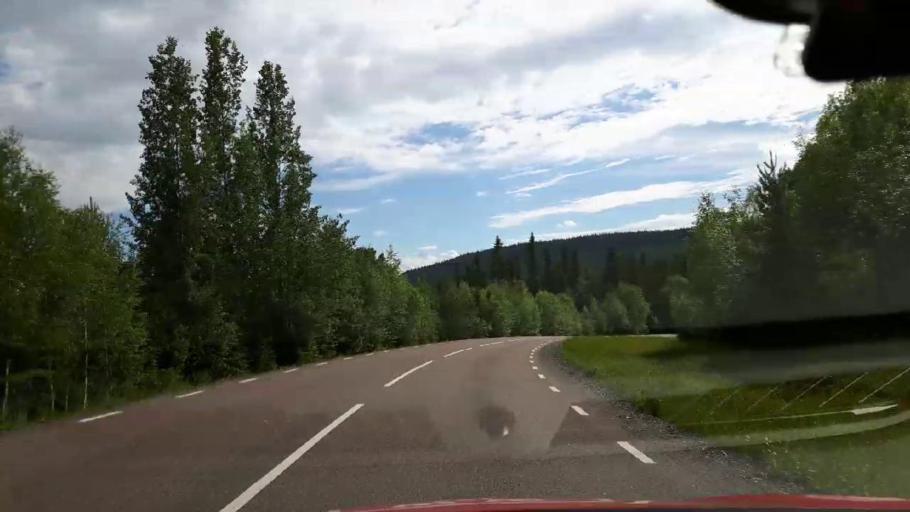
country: SE
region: Jaemtland
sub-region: Krokoms Kommun
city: Valla
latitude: 63.9360
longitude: 14.2213
